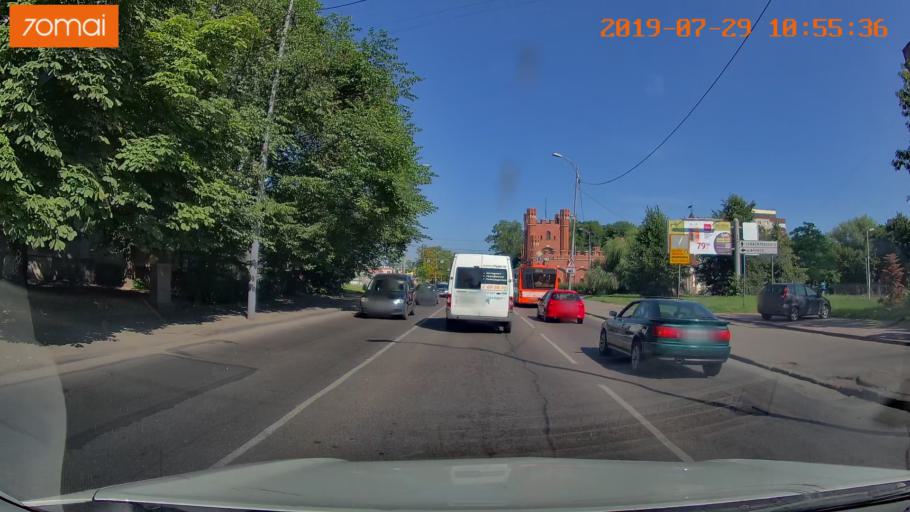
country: RU
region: Kaliningrad
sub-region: Gorod Kaliningrad
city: Kaliningrad
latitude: 54.7126
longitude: 20.5365
